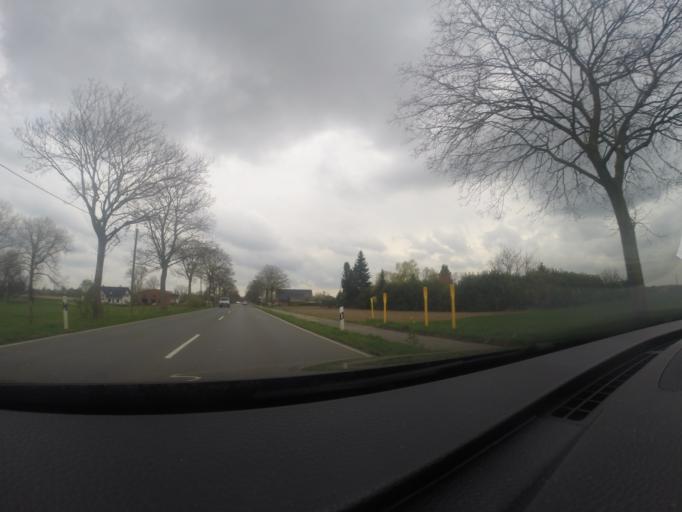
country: DE
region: North Rhine-Westphalia
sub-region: Regierungsbezirk Dusseldorf
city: Alpen
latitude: 51.6131
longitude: 6.5099
